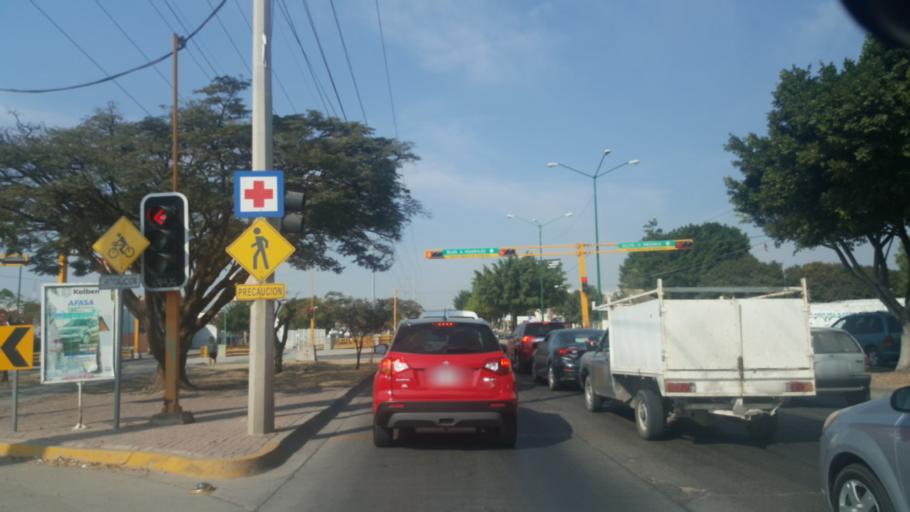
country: MX
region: Guanajuato
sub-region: Leon
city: Medina
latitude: 21.1445
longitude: -101.6442
